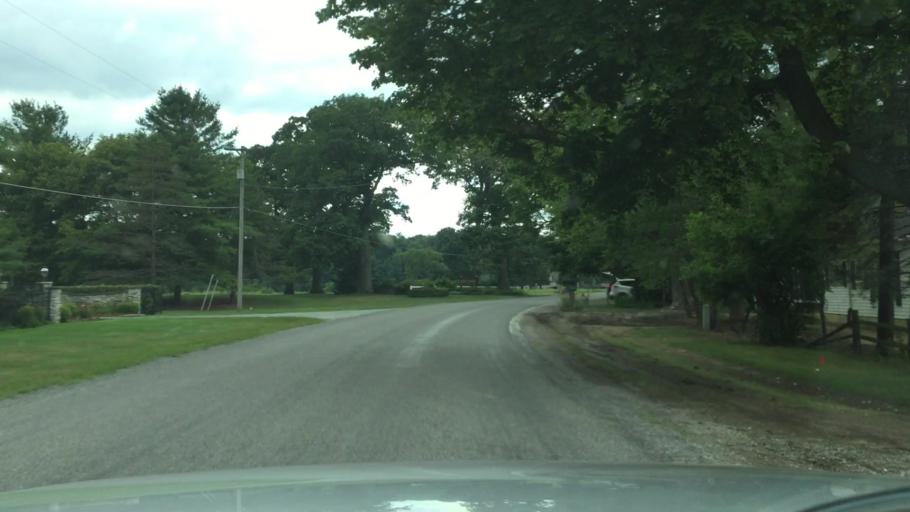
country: US
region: Michigan
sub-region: Saginaw County
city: Frankenmuth
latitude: 43.3212
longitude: -83.8051
